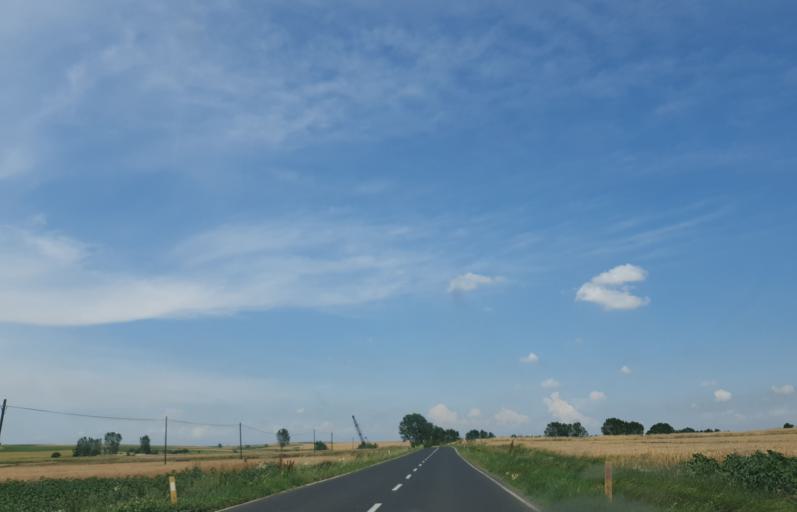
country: TR
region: Tekirdag
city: Muratli
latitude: 41.2242
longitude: 27.5545
